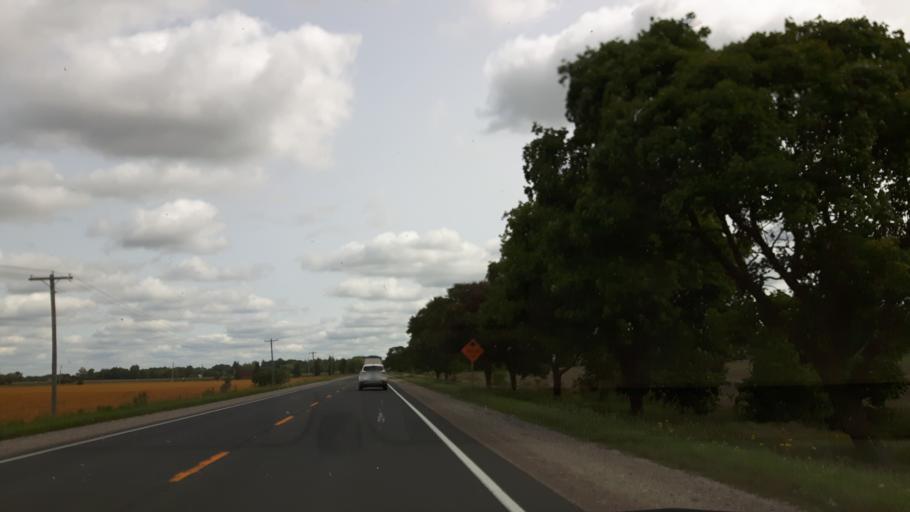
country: CA
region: Ontario
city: Huron East
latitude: 43.5643
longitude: -81.4174
